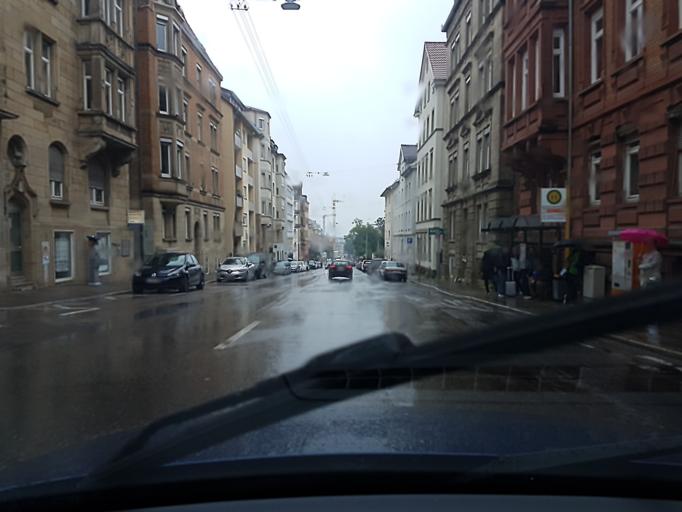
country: DE
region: Baden-Wuerttemberg
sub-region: Regierungsbezirk Stuttgart
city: Stuttgart
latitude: 48.7796
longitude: 9.1601
